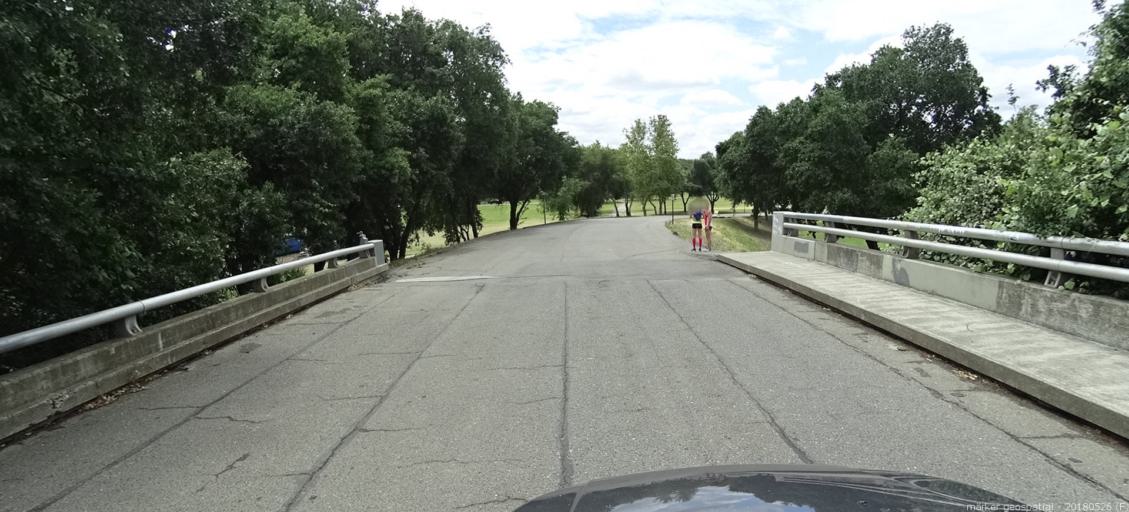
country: US
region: California
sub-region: Sacramento County
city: Sacramento
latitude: 38.6068
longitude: -121.5021
